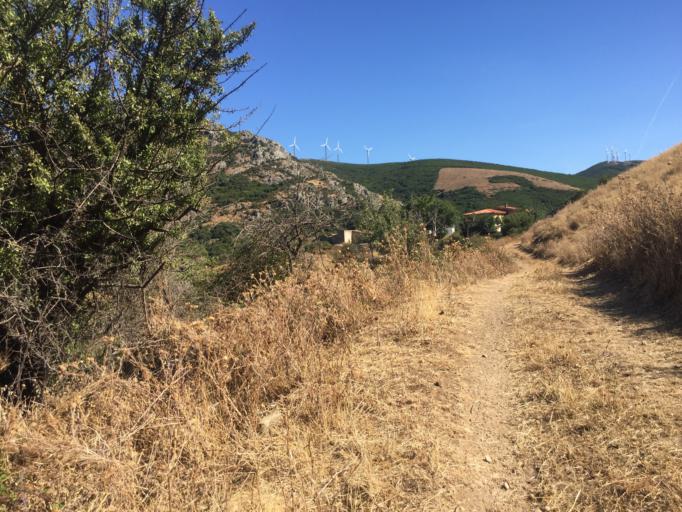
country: IT
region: Sardinia
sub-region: Provincia di Olbia-Tempio
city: Aggius
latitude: 40.9523
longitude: 8.9906
